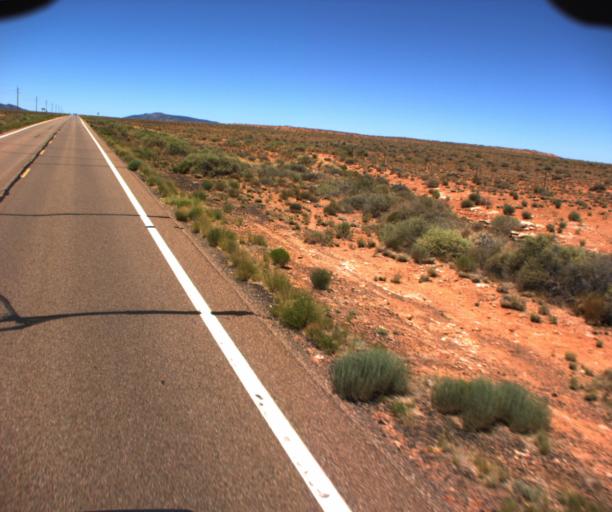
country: US
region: Arizona
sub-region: Coconino County
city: LeChee
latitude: 34.9477
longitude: -110.7672
